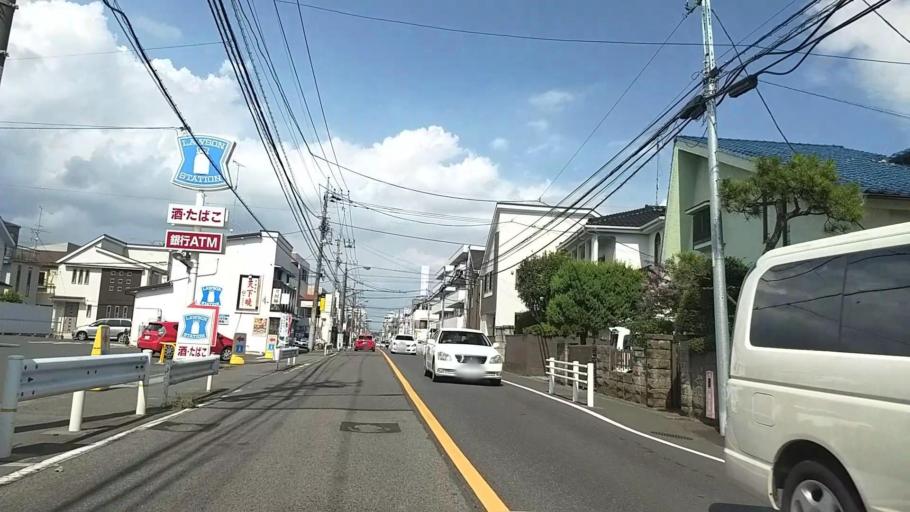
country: JP
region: Tokyo
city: Hachioji
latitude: 35.6518
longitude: 139.3068
